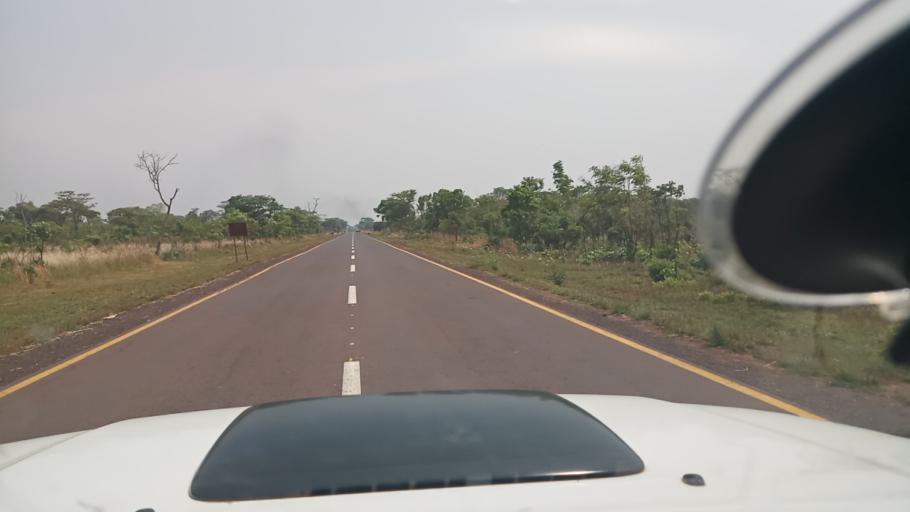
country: ZM
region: Luapula
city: Mwense
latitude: -10.8079
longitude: 28.2333
